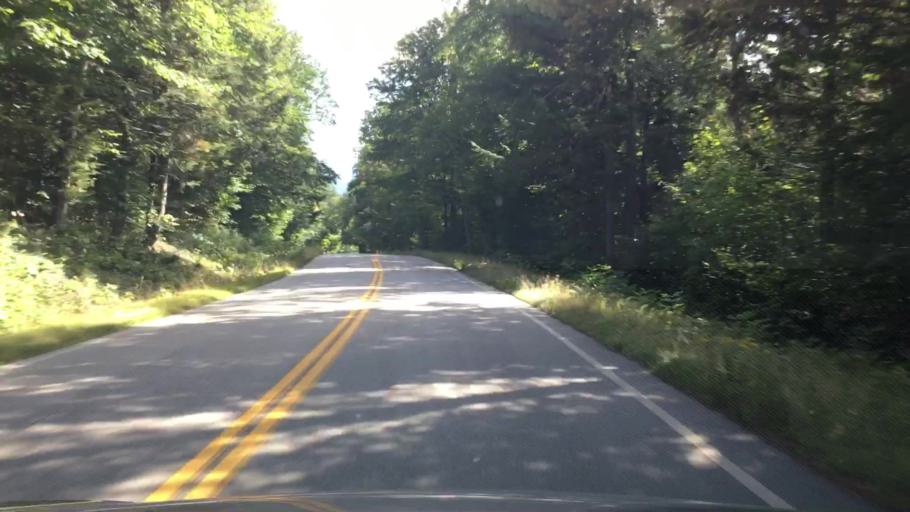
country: US
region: New Hampshire
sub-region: Carroll County
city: Tamworth
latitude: 44.0144
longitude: -71.3207
